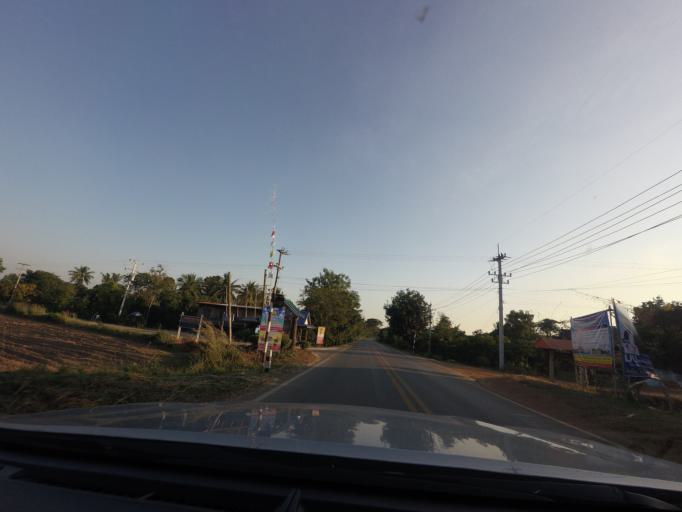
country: TH
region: Sukhothai
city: Sawankhalok
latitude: 17.3426
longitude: 99.8263
